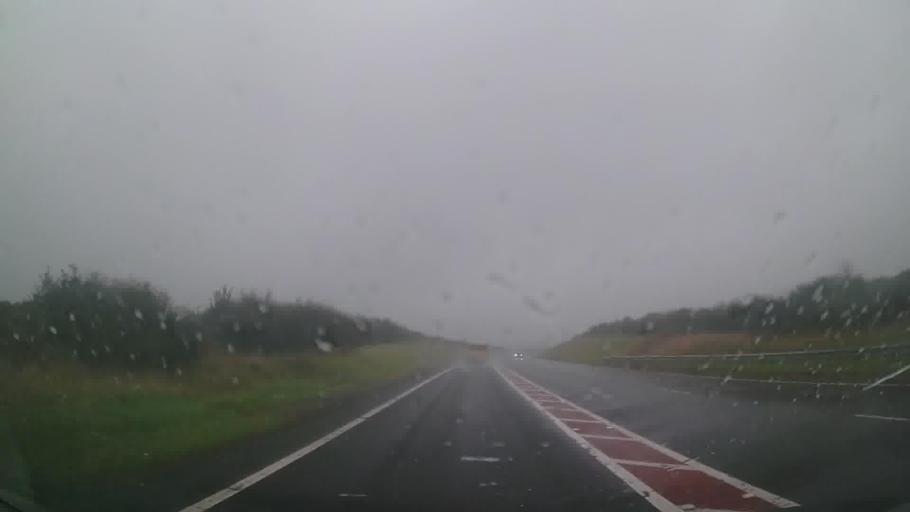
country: GB
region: Wales
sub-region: Carmarthenshire
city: Whitland
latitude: 51.7807
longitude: -4.6056
